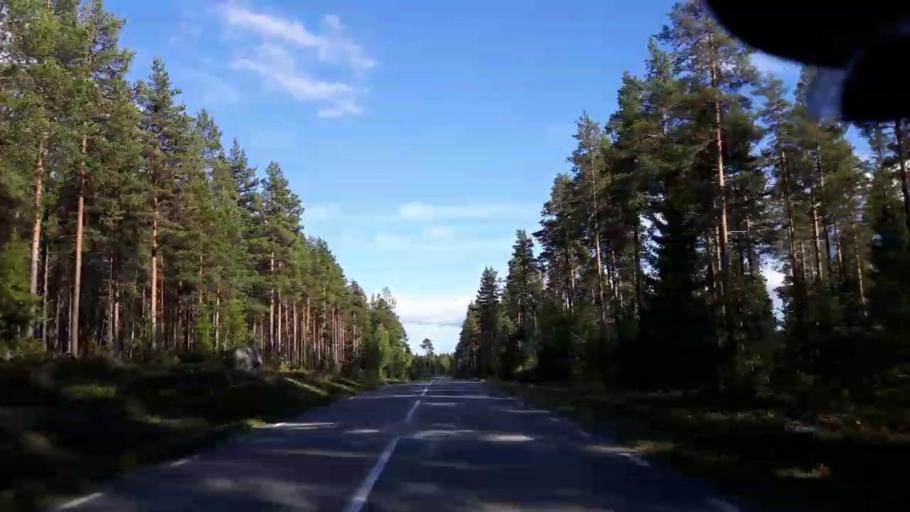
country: SE
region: Jaemtland
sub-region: Stroemsunds Kommun
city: Stroemsund
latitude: 63.3772
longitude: 15.5626
